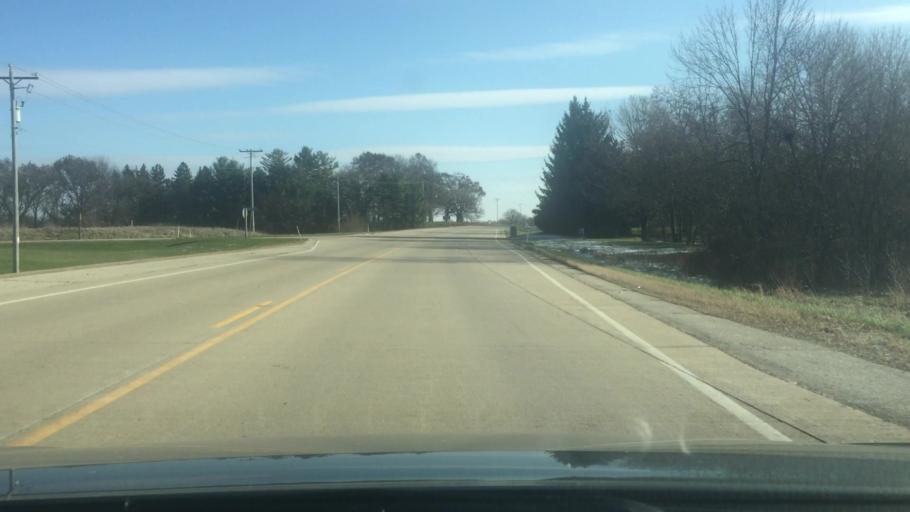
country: US
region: Wisconsin
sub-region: Jefferson County
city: Fort Atkinson
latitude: 42.9558
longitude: -88.8854
